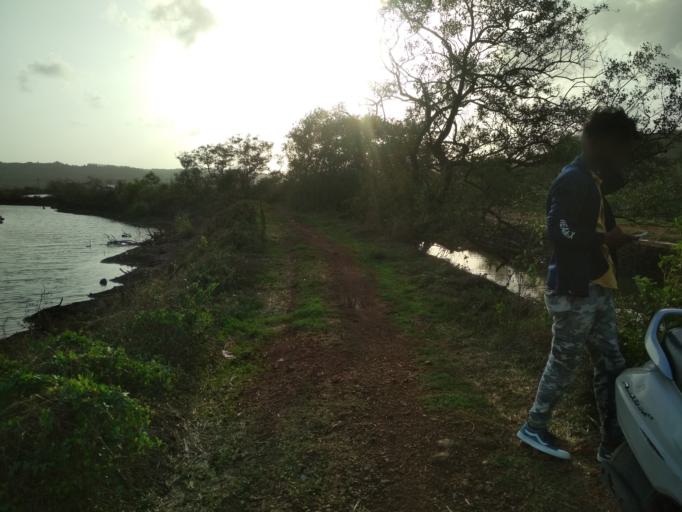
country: IN
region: Goa
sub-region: North Goa
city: Serula
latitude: 15.5293
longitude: 73.8610
